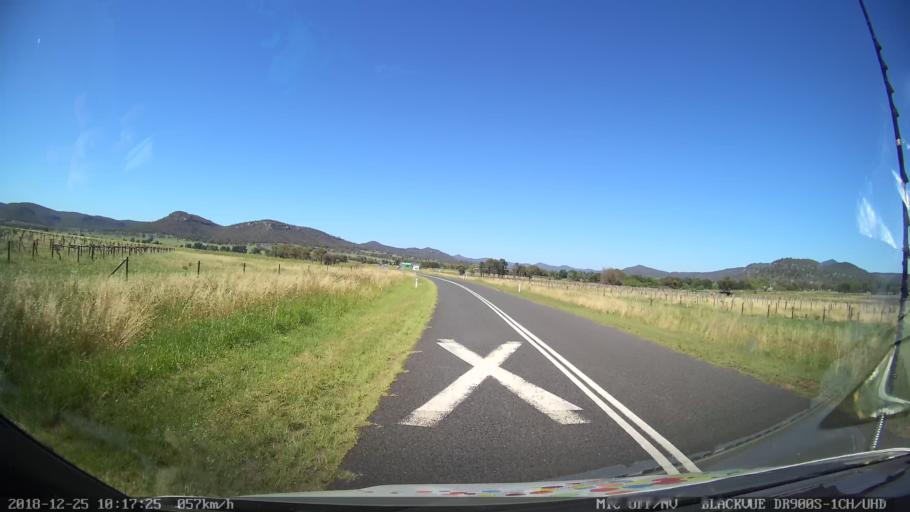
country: AU
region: New South Wales
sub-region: Muswellbrook
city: Denman
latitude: -32.3424
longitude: 150.5781
